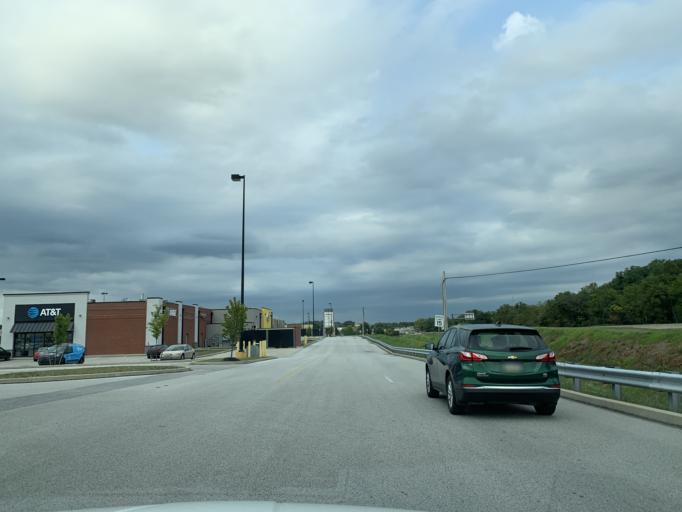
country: US
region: Pennsylvania
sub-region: York County
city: West York
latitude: 39.9685
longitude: -76.7701
